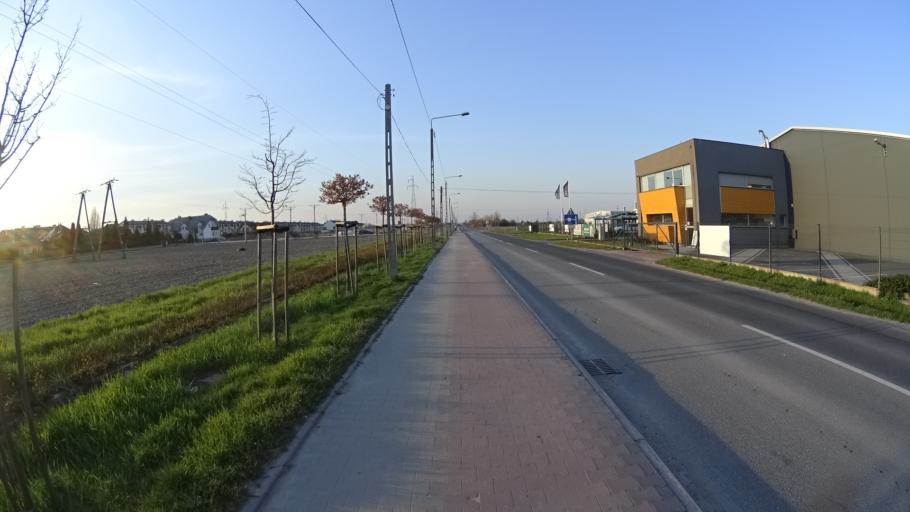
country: PL
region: Masovian Voivodeship
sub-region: Powiat warszawski zachodni
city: Ozarow Mazowiecki
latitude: 52.2120
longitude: 20.8109
